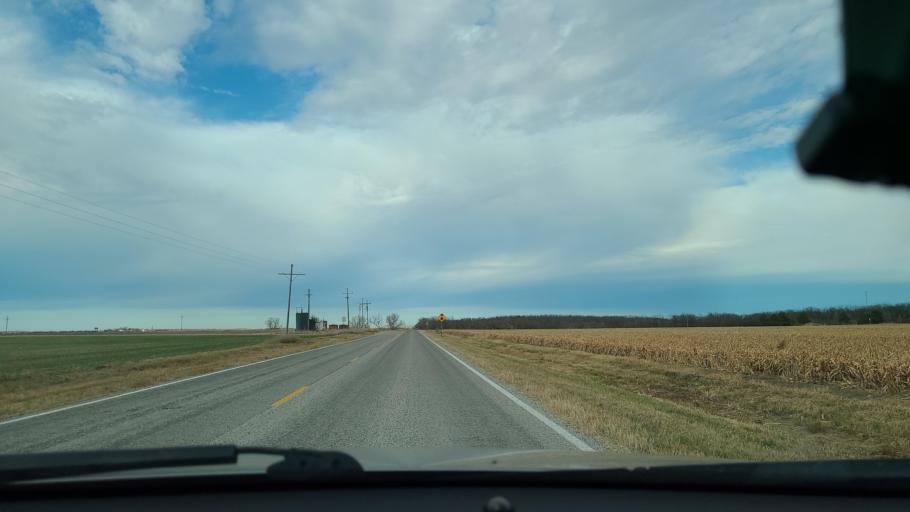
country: US
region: Kansas
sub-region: McPherson County
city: Inman
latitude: 38.3747
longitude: -97.9244
